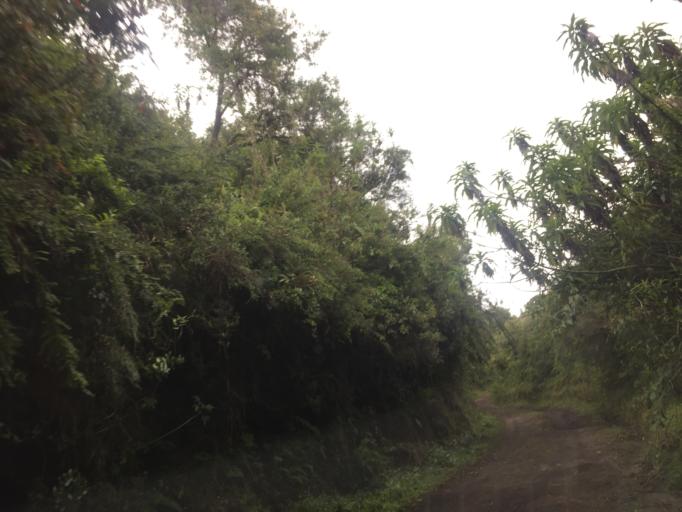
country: EC
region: Imbabura
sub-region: Canton Otavalo
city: Otavalo
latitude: 0.0849
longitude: -78.2974
